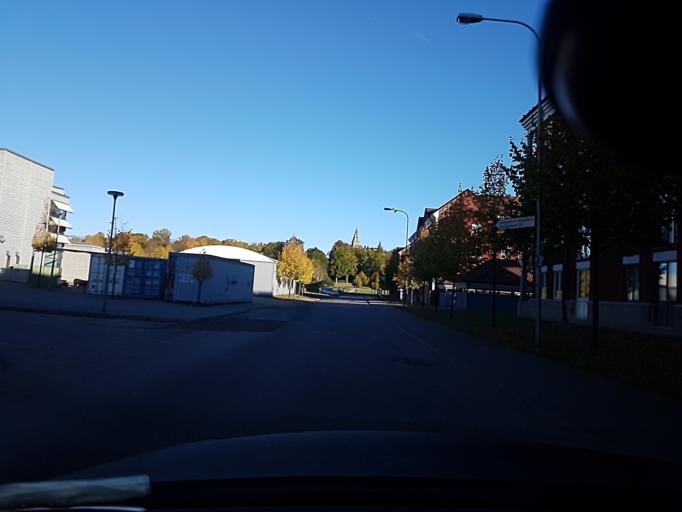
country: SE
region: Kronoberg
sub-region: Vaxjo Kommun
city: Vaexjoe
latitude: 56.8536
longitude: 14.8347
